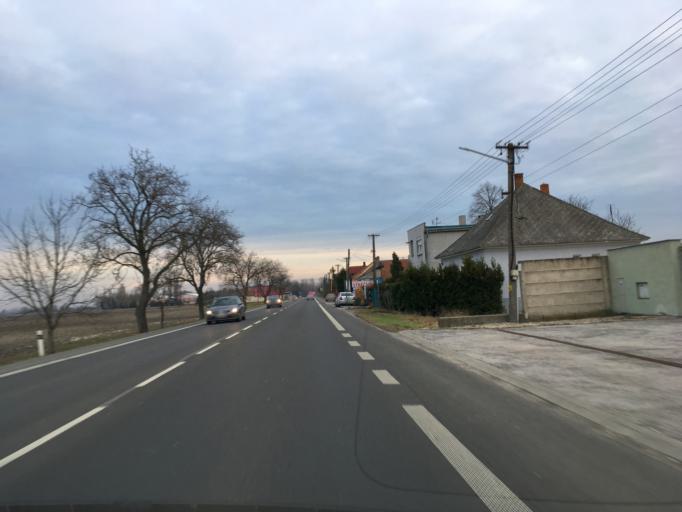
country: SK
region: Trnavsky
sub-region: Okres Dunajska Streda
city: Velky Meder
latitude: 47.9466
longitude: 17.7134
